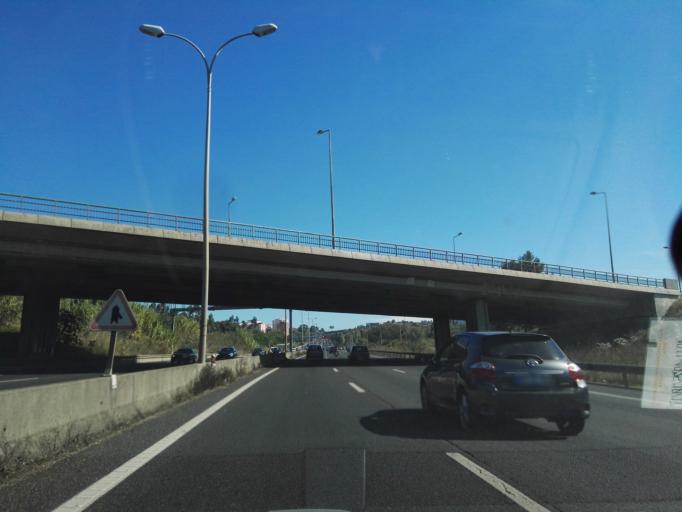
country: PT
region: Lisbon
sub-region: Sintra
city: Queluz
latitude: 38.7490
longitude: -9.2475
